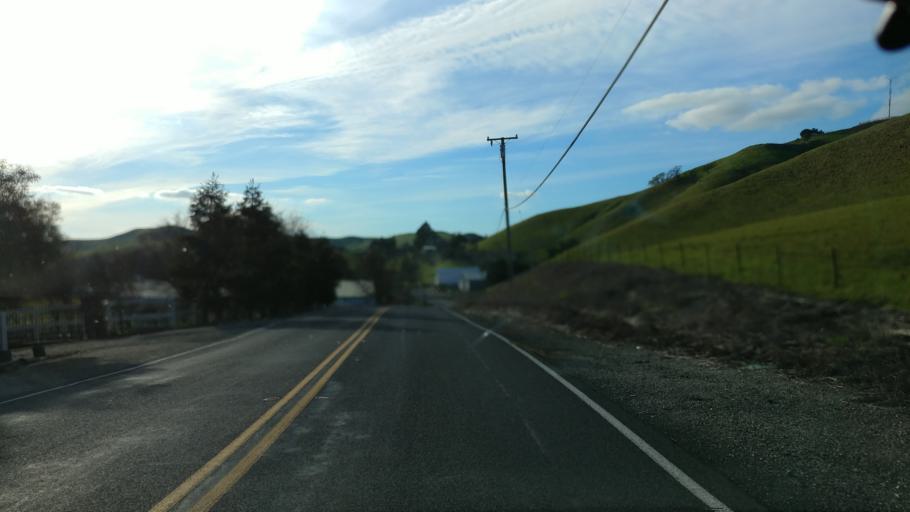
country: US
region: California
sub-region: Contra Costa County
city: Blackhawk
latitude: 37.7758
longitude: -121.8513
